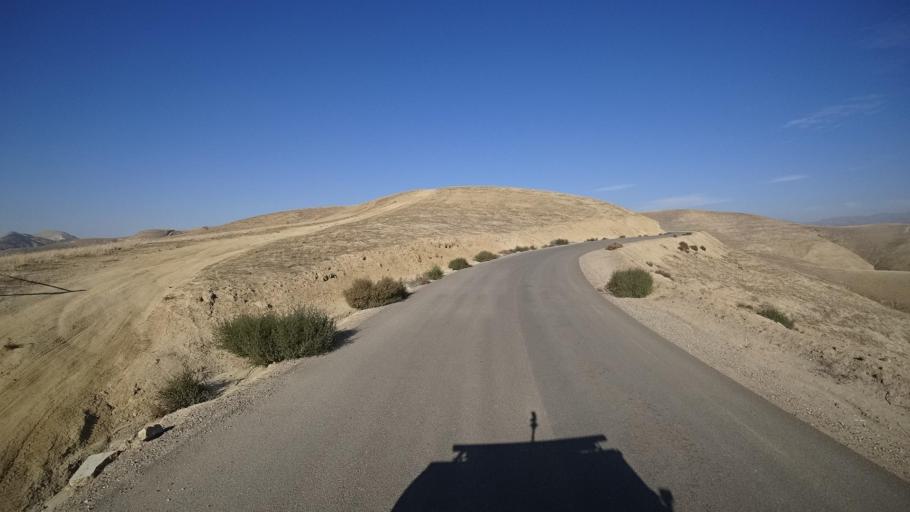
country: US
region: California
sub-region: Kern County
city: Oildale
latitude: 35.4630
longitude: -118.8717
